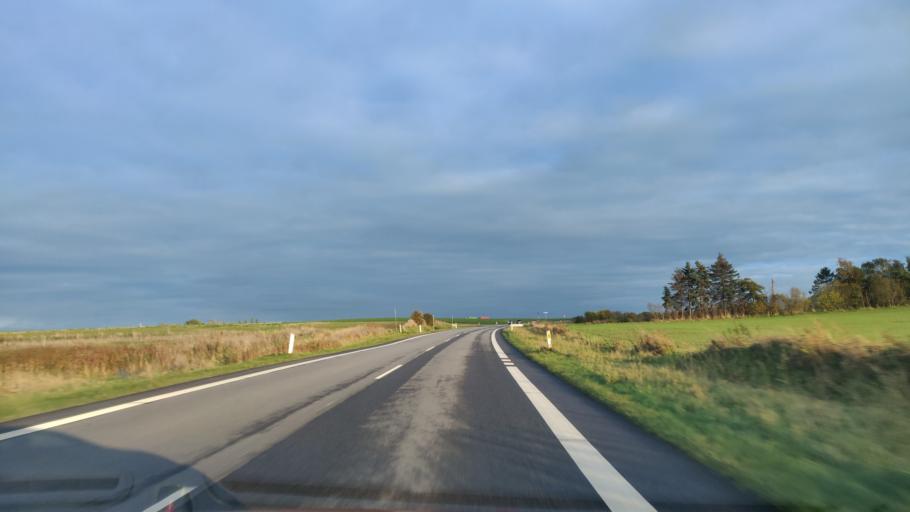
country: DK
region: Zealand
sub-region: Holbaek Kommune
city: Vipperod
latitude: 55.6837
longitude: 11.7269
